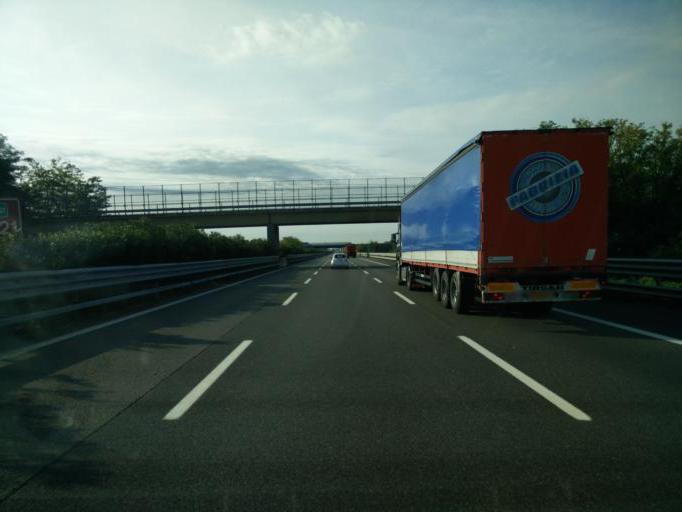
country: IT
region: Lombardy
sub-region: Provincia di Brescia
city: San Zeno Naviglio
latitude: 45.4864
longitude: 10.2259
